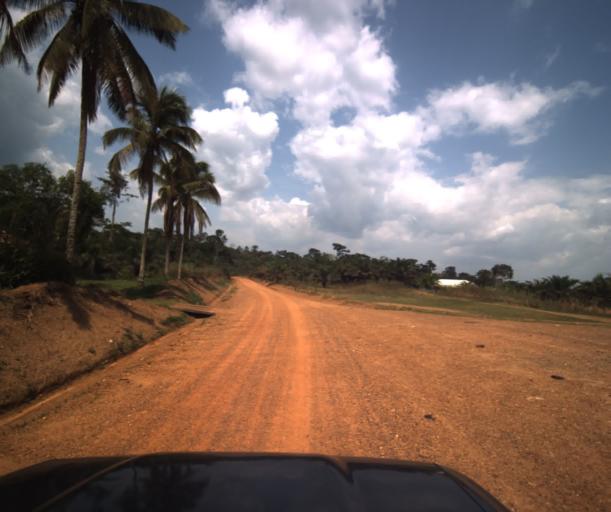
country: CM
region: Centre
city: Akono
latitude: 3.5499
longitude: 11.0559
